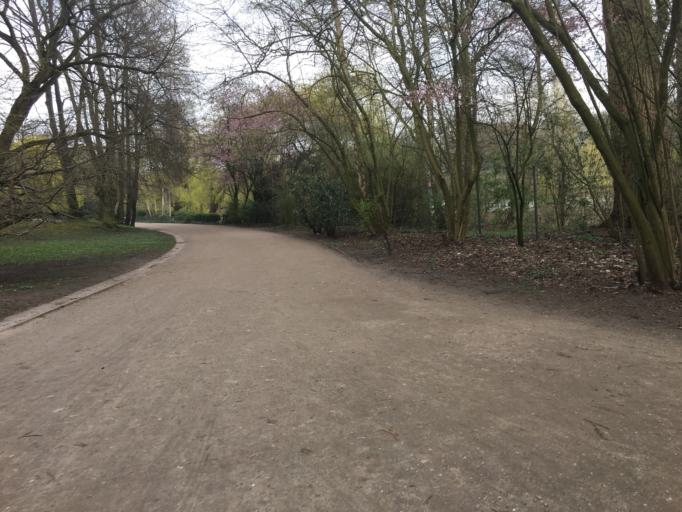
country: DE
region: Schleswig-Holstein
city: Kiel
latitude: 54.3276
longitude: 10.1219
